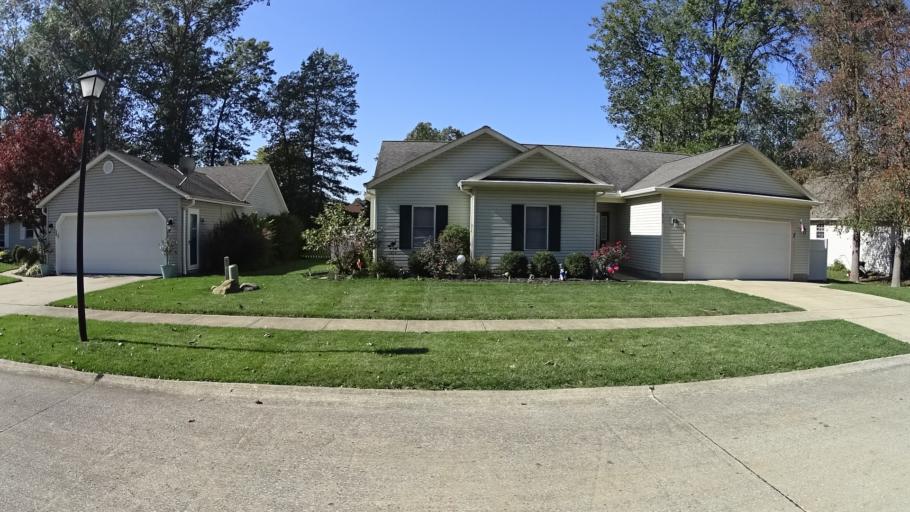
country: US
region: Ohio
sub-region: Lorain County
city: Vermilion-on-the-Lake
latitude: 41.4216
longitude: -82.3185
